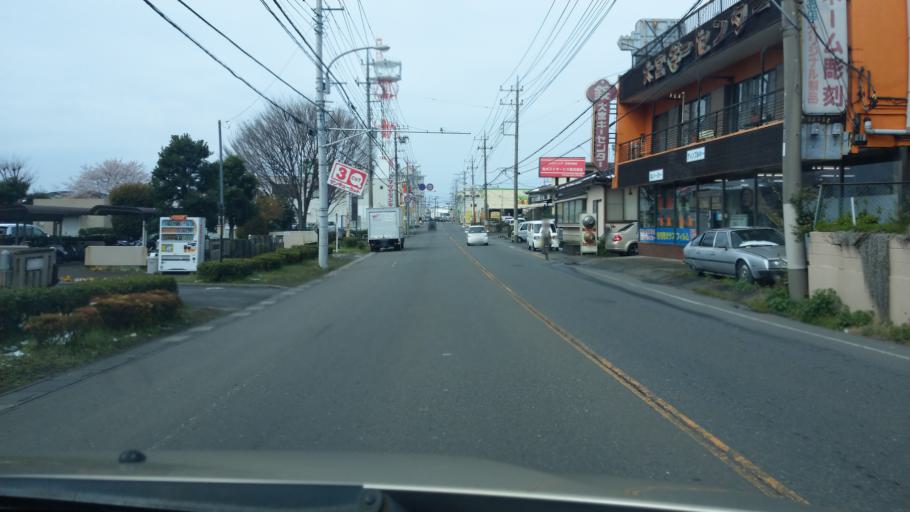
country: JP
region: Saitama
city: Yono
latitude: 35.9127
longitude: 139.5800
